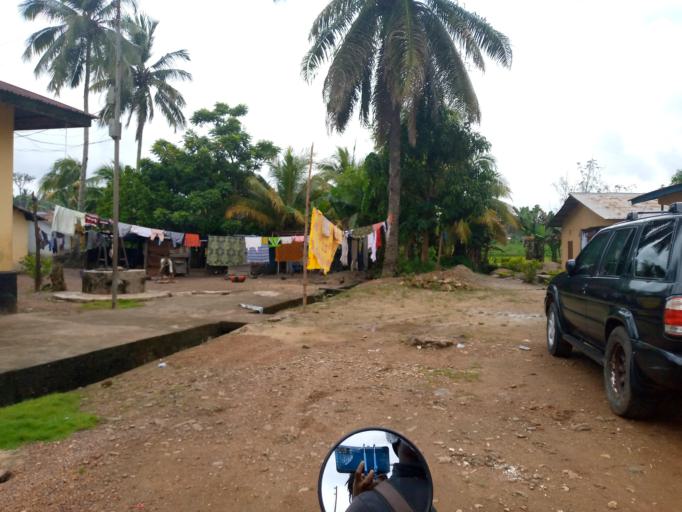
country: SL
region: Eastern Province
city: Kenema
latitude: 7.8637
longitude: -11.1911
